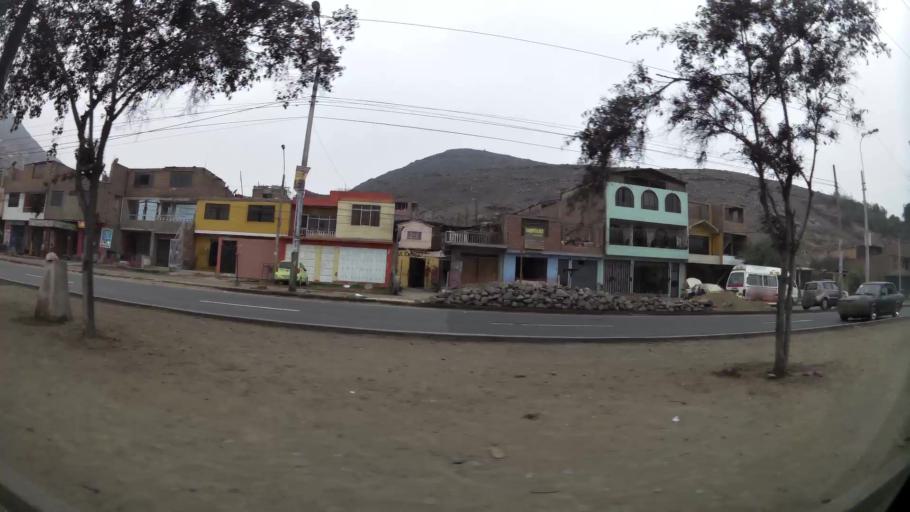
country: PE
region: Lima
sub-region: Lima
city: Urb. Santo Domingo
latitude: -11.9088
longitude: -77.0353
